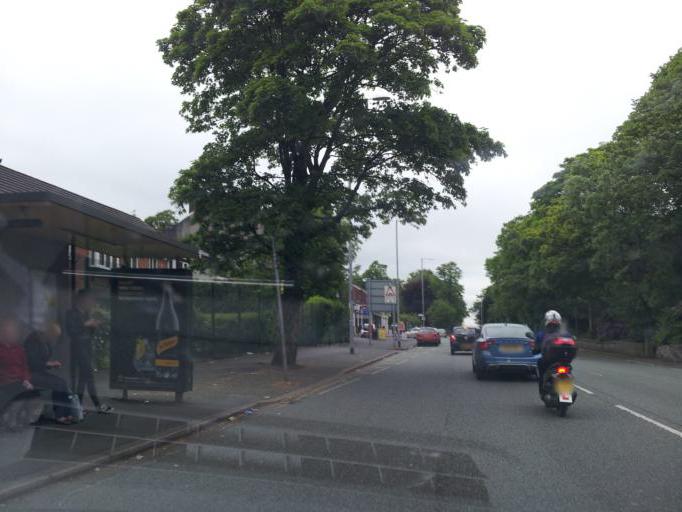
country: GB
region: England
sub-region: Manchester
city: Crumpsall
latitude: 53.5186
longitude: -2.2488
